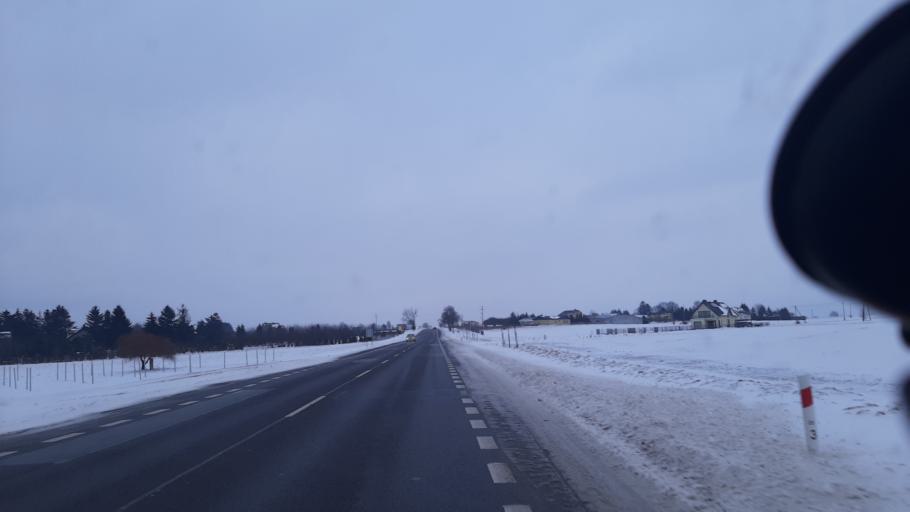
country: PL
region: Lublin Voivodeship
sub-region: Powiat pulawski
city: Kurow
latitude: 51.3840
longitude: 22.2181
